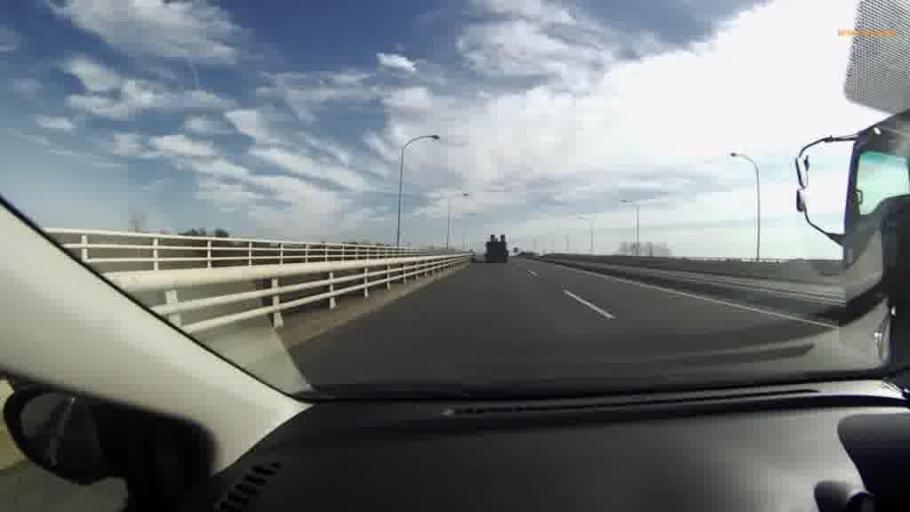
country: JP
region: Hokkaido
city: Kushiro
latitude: 43.0218
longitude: 144.2687
